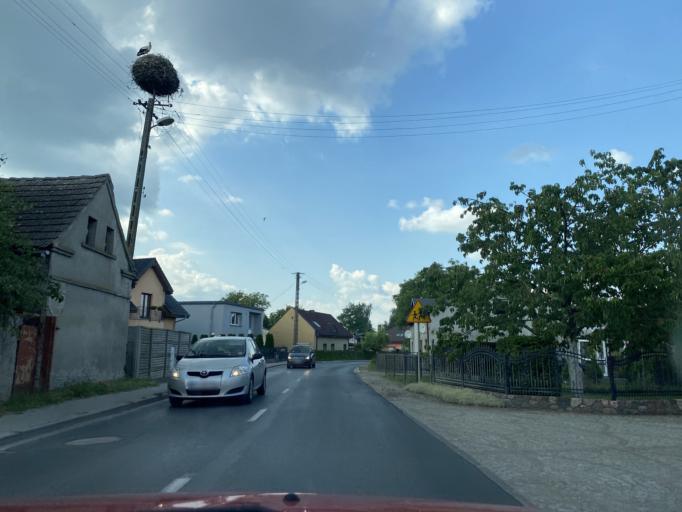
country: PL
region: Greater Poland Voivodeship
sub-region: Powiat poznanski
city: Dopiewo
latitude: 52.3682
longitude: 16.7361
